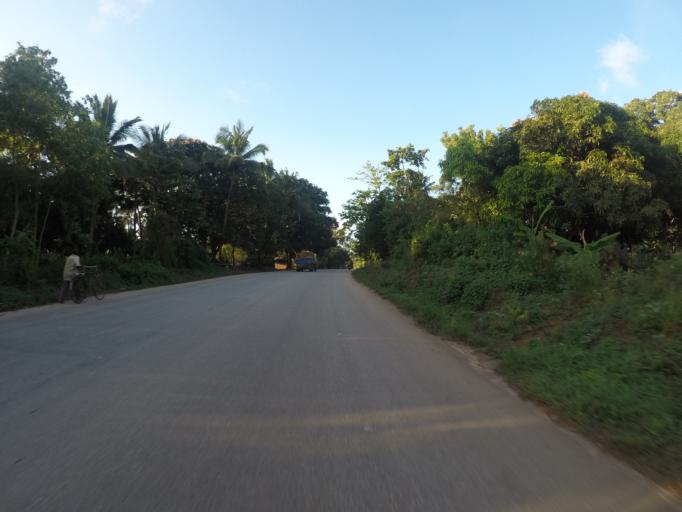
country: TZ
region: Zanzibar North
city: Kijini
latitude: -5.8189
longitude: 39.2914
